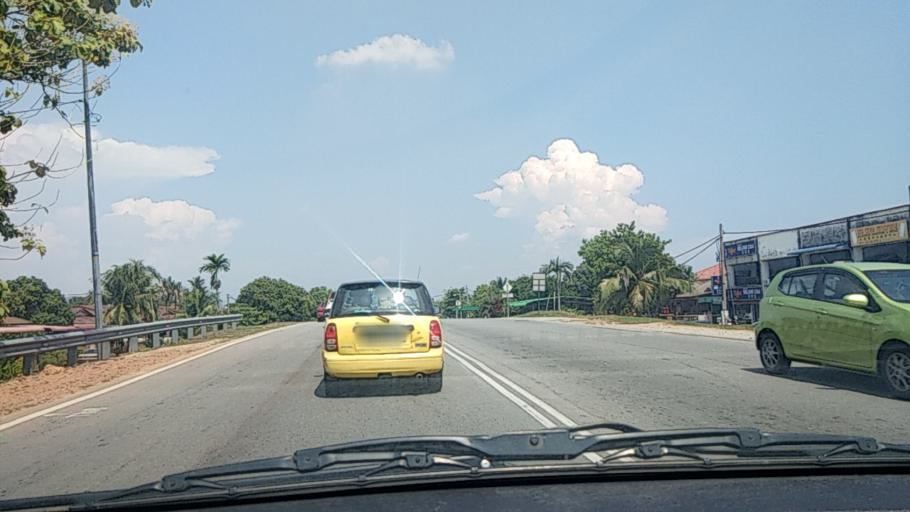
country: MY
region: Kedah
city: Sungai Petani
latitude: 5.6416
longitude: 100.5067
